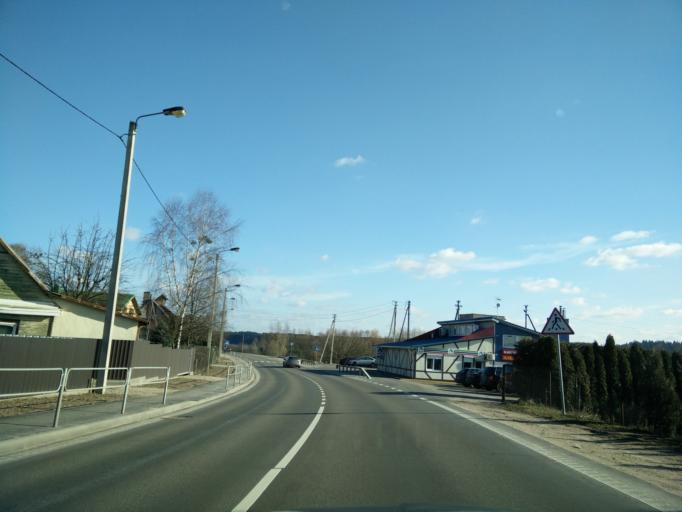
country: LT
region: Kauno apskritis
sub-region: Kauno rajonas
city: Akademija (Kaunas)
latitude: 54.9233
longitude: 23.7939
